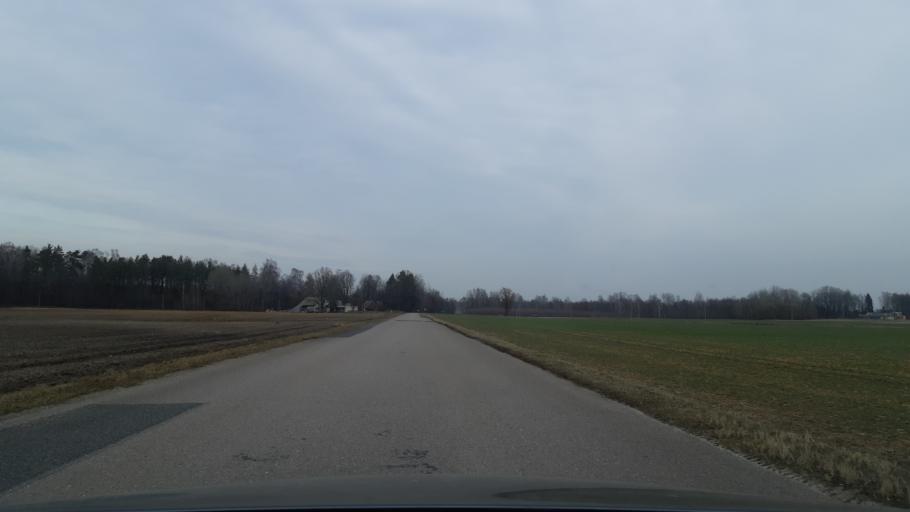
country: LT
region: Marijampoles apskritis
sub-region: Marijampole Municipality
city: Marijampole
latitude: 54.7292
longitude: 23.3376
